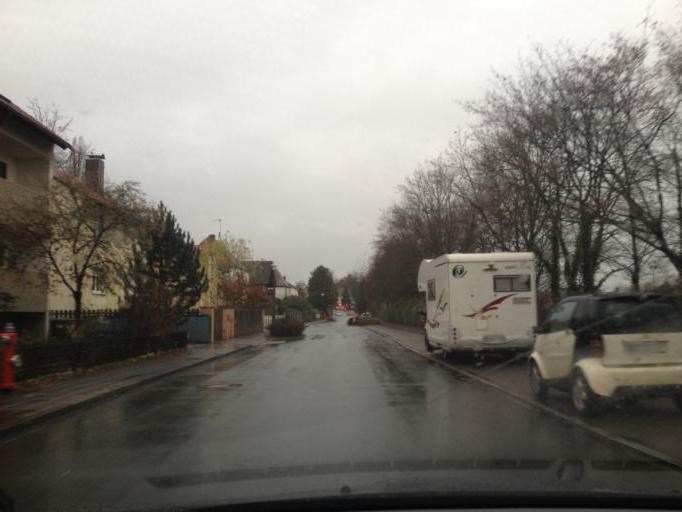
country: DE
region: Bavaria
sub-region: Regierungsbezirk Mittelfranken
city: Schwaig
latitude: 49.4745
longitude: 11.2027
